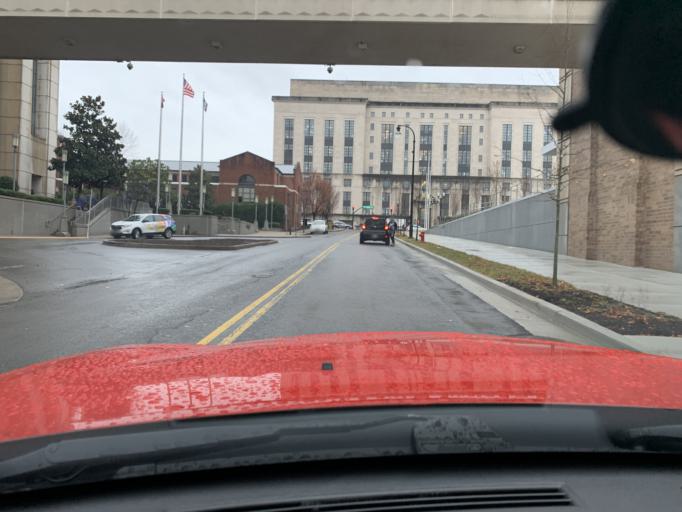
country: US
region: Tennessee
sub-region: Davidson County
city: Nashville
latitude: 36.1685
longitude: -86.7792
